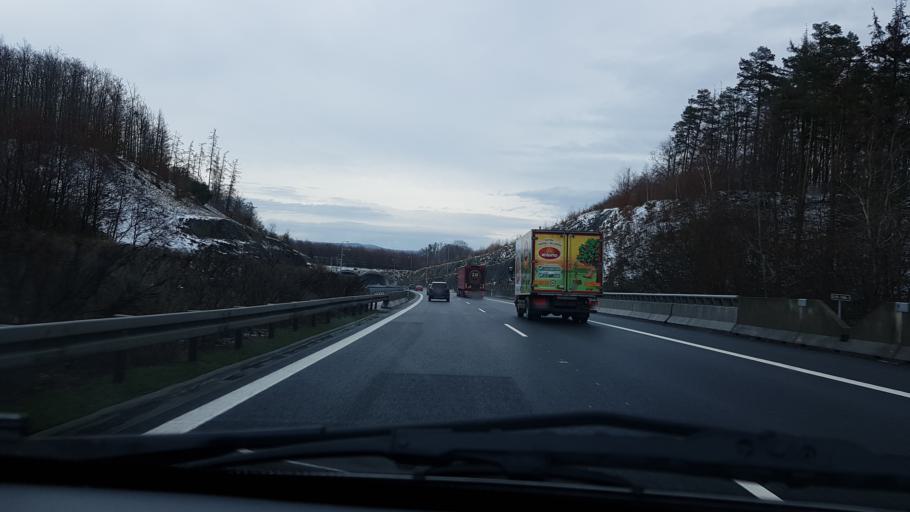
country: CZ
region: Olomoucky
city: Dolni Ujezd
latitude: 49.5527
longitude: 17.5305
